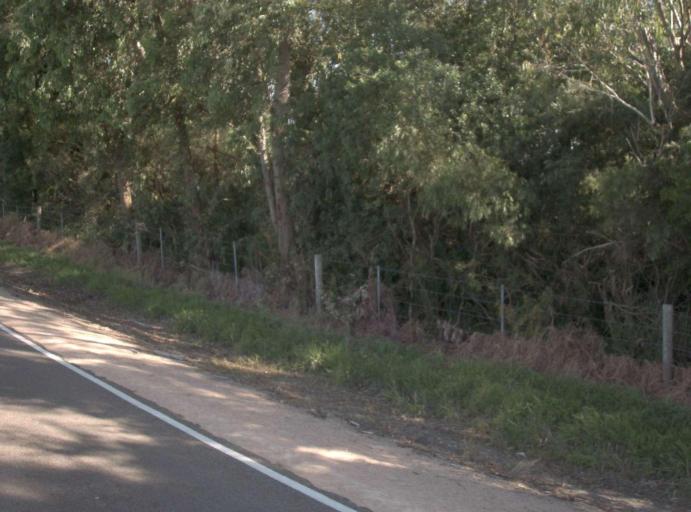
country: AU
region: Victoria
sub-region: East Gippsland
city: Lakes Entrance
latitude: -37.7236
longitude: 148.4970
